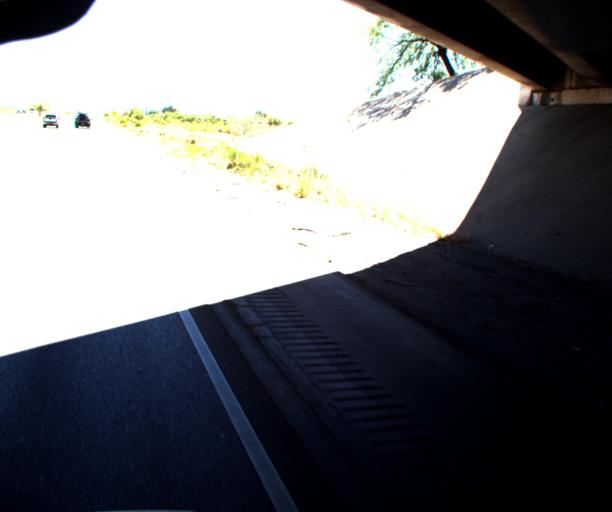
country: US
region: Arizona
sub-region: Pima County
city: Summit
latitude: 32.1037
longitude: -110.8410
